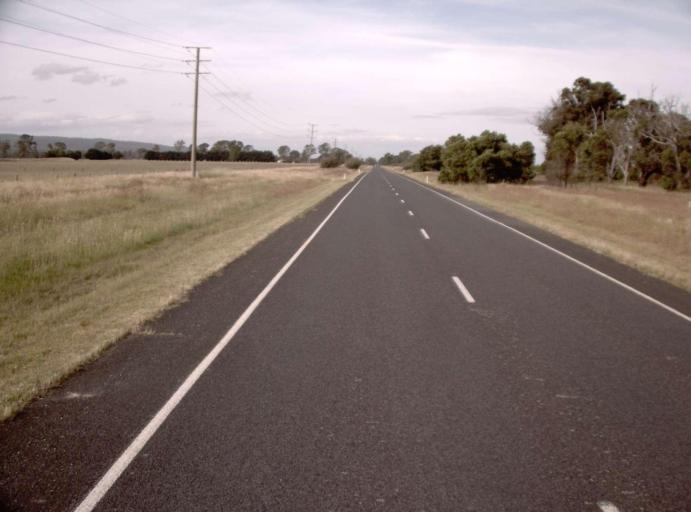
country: AU
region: Victoria
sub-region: Latrobe
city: Traralgon
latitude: -38.0852
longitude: 146.6050
